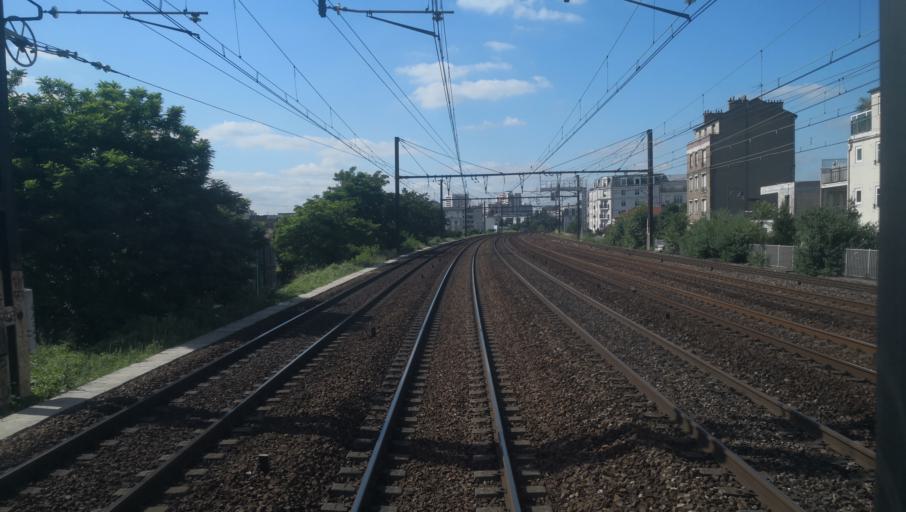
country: FR
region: Ile-de-France
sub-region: Departement du Val-de-Marne
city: Alfortville
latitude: 48.8124
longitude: 2.4192
